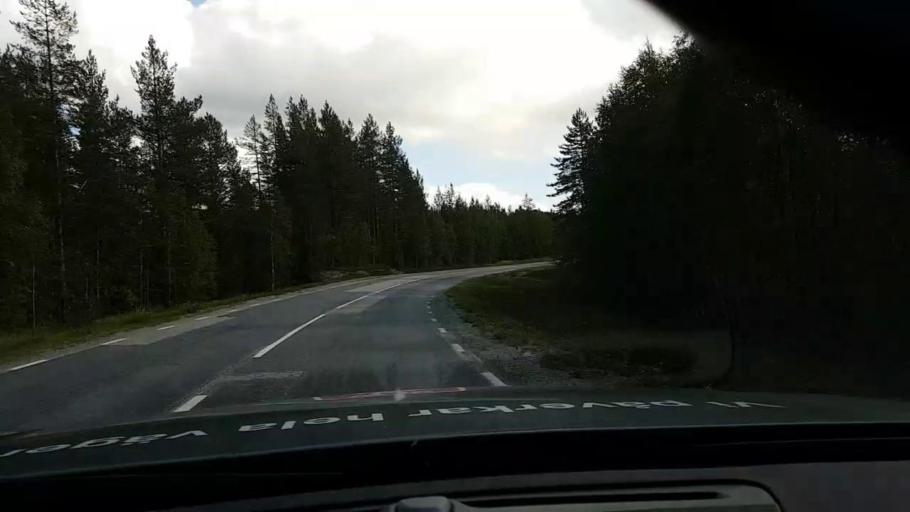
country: SE
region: Vaesterbotten
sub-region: Asele Kommun
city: Asele
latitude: 63.7914
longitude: 17.5834
